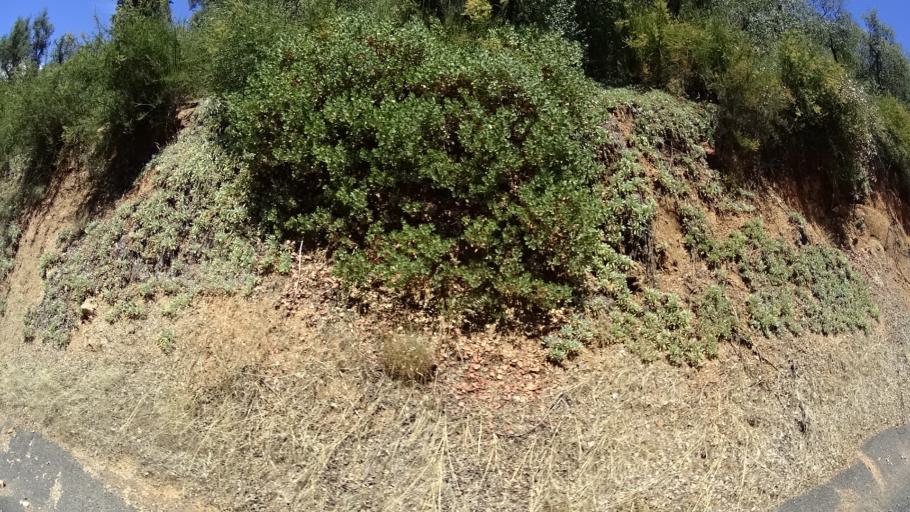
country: US
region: California
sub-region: Calaveras County
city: Mountain Ranch
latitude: 38.2176
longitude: -120.4668
